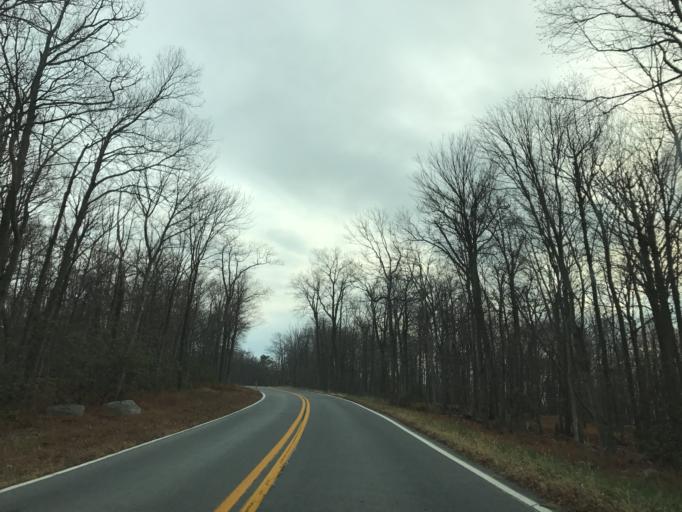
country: US
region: Maryland
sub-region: Frederick County
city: Myersville
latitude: 39.4957
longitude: -77.5004
